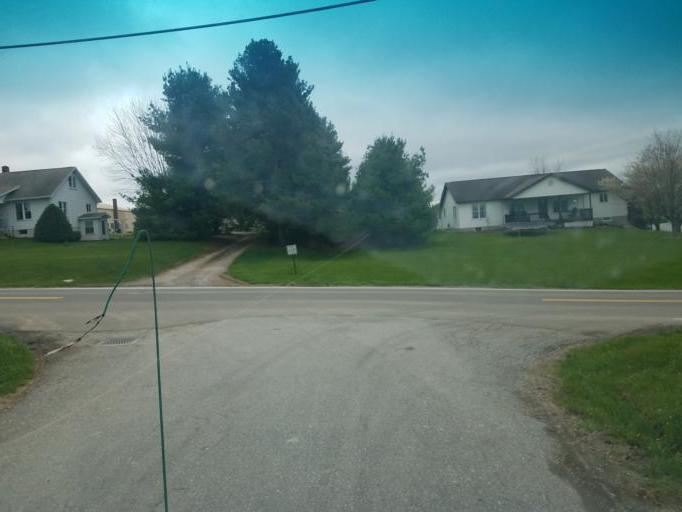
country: US
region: Ohio
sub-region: Tuscarawas County
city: Sugarcreek
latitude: 40.6177
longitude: -81.7214
